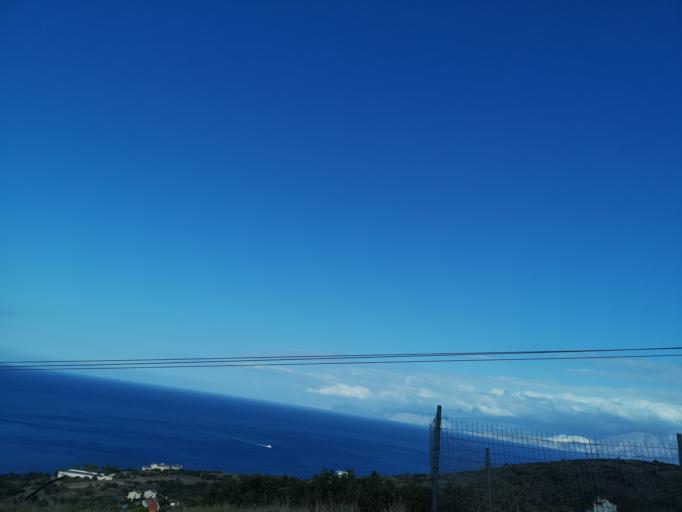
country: GR
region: Crete
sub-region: Nomos Lasithiou
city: Skhisma
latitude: 35.2337
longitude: 25.7282
